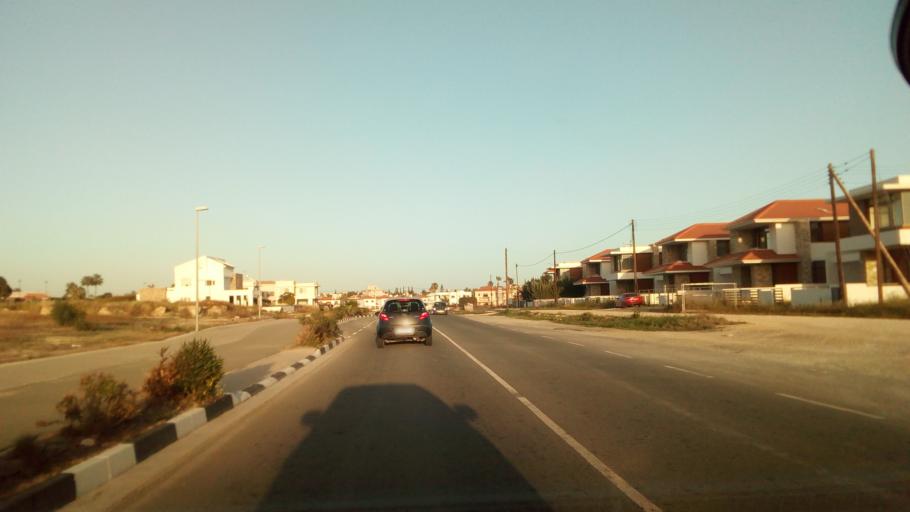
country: CY
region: Larnaka
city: Voroklini
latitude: 34.9753
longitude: 33.6711
